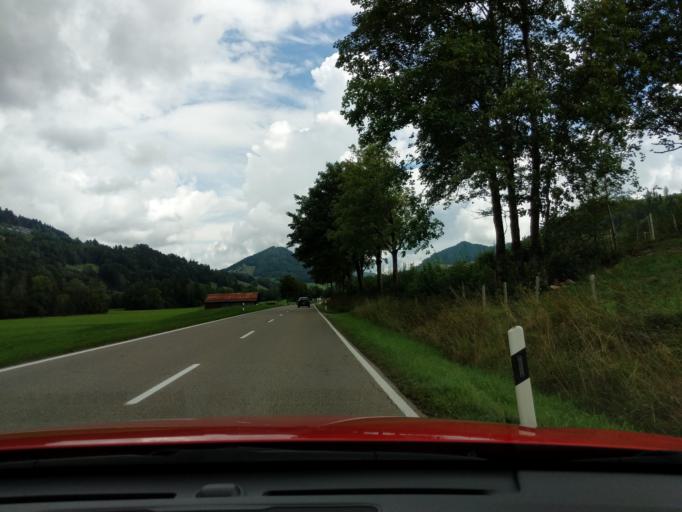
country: DE
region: Bavaria
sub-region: Swabia
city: Oberstaufen
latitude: 47.5334
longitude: 9.9923
